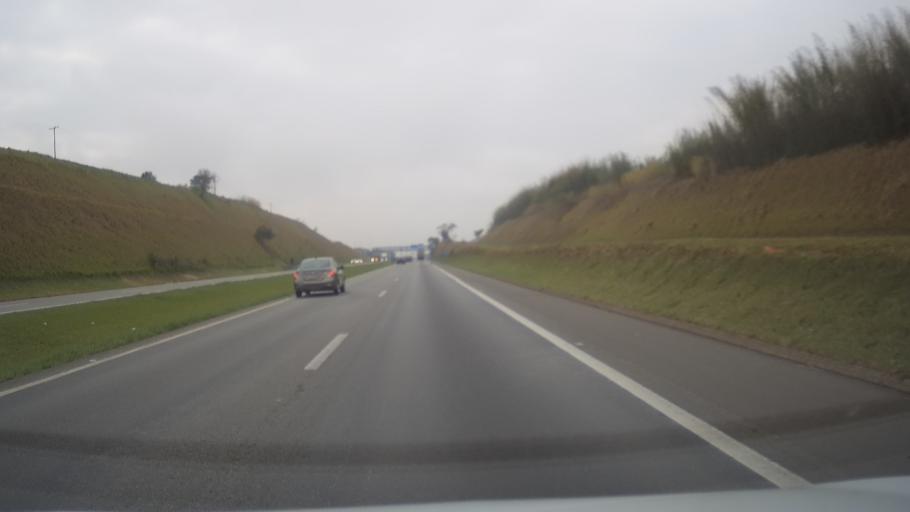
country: BR
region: Sao Paulo
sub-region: Atibaia
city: Atibaia
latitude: -23.0848
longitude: -46.6329
